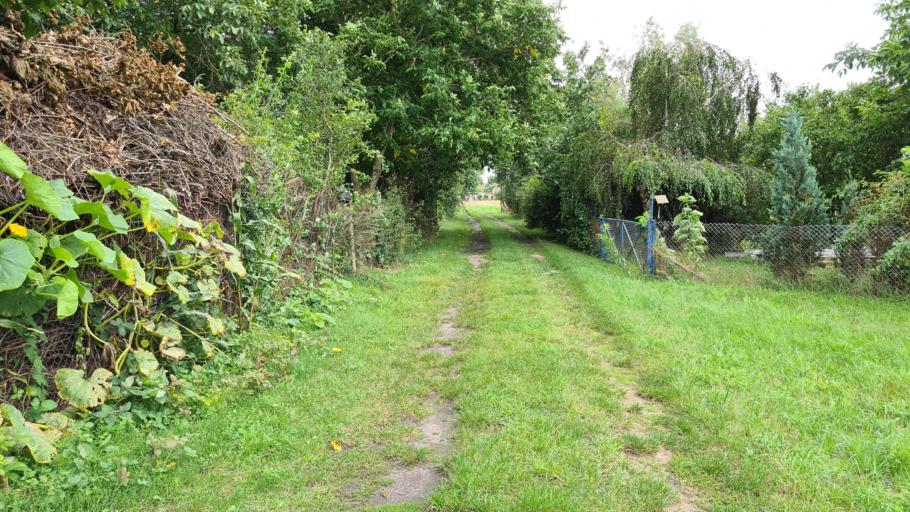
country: DE
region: Brandenburg
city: Doberlug-Kirchhain
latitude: 51.6438
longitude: 13.5592
